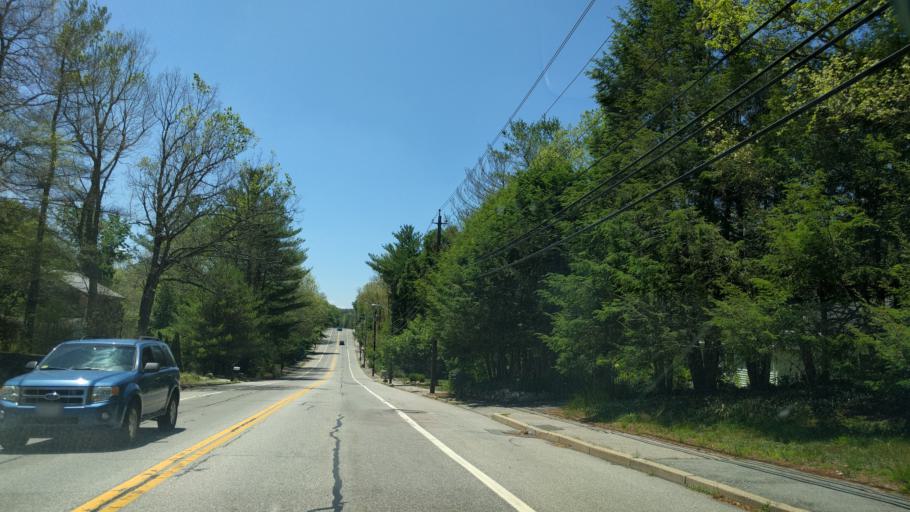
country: US
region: Massachusetts
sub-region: Worcester County
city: Millville
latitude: 42.0023
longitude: -71.5920
